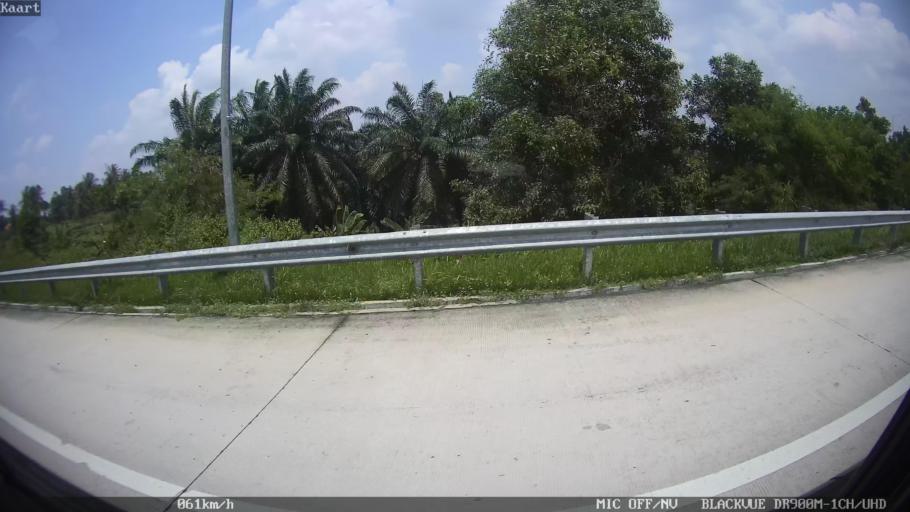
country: ID
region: Lampung
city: Natar
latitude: -5.2753
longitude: 105.2154
